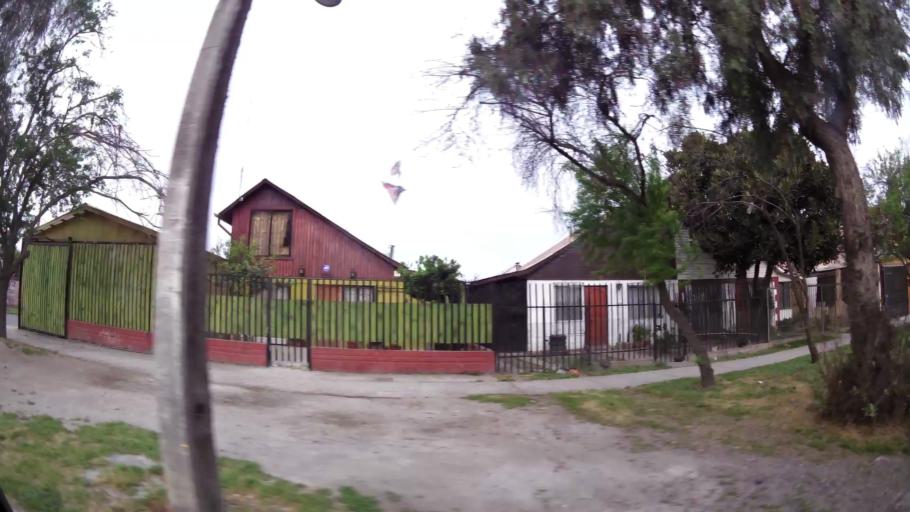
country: CL
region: Santiago Metropolitan
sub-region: Provincia de Santiago
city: Lo Prado
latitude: -33.5155
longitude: -70.7778
